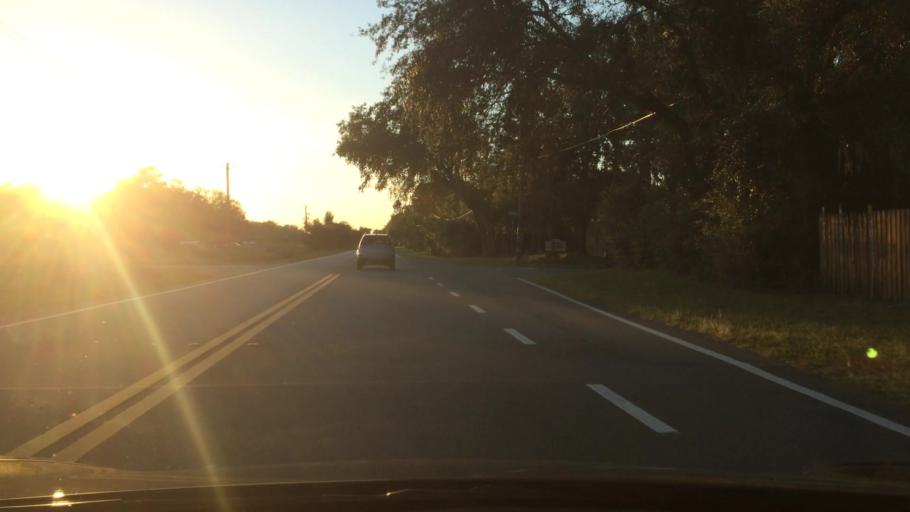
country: US
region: Florida
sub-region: Hillsborough County
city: Lutz
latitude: 28.1714
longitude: -82.4181
